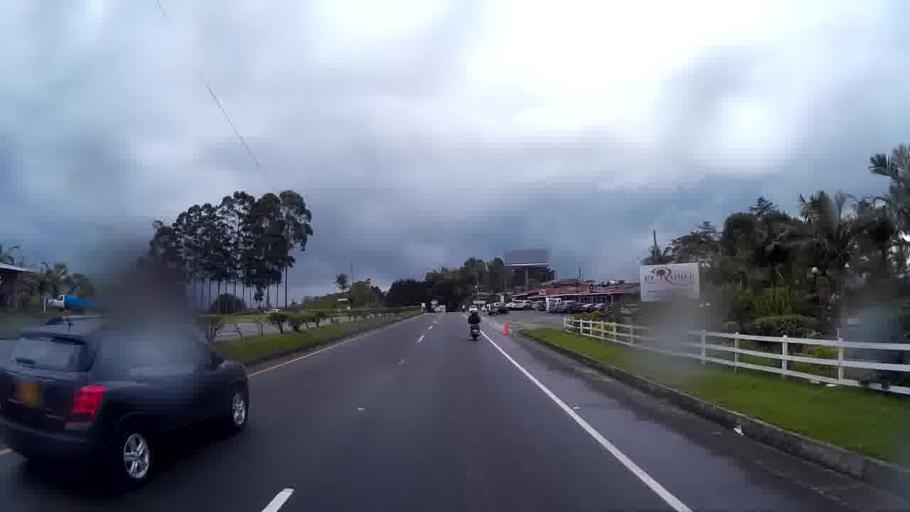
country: CO
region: Quindio
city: Salento
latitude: 4.6635
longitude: -75.5960
